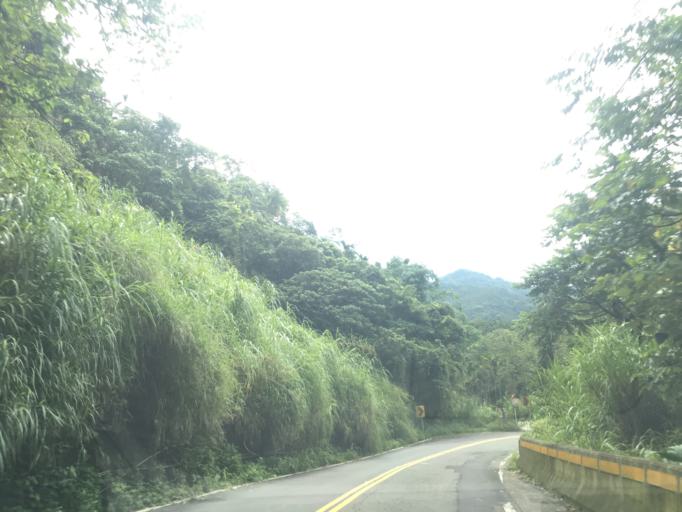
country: TW
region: Taiwan
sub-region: Yunlin
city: Douliu
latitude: 23.5644
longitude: 120.5752
